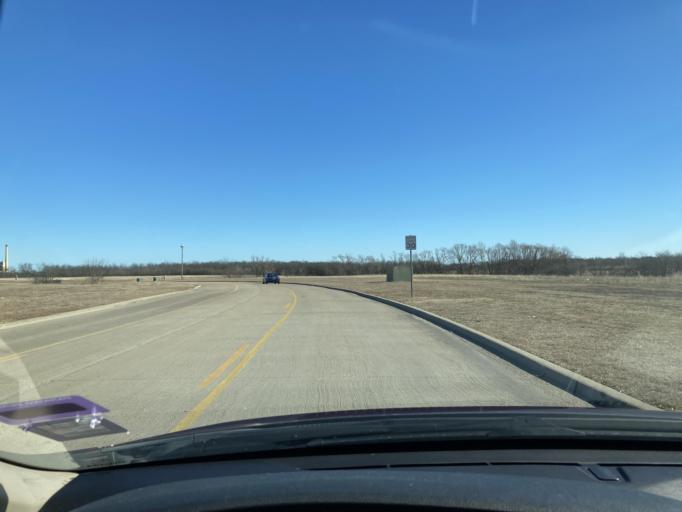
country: US
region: Texas
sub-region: Navarro County
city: Corsicana
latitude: 32.0640
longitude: -96.4468
